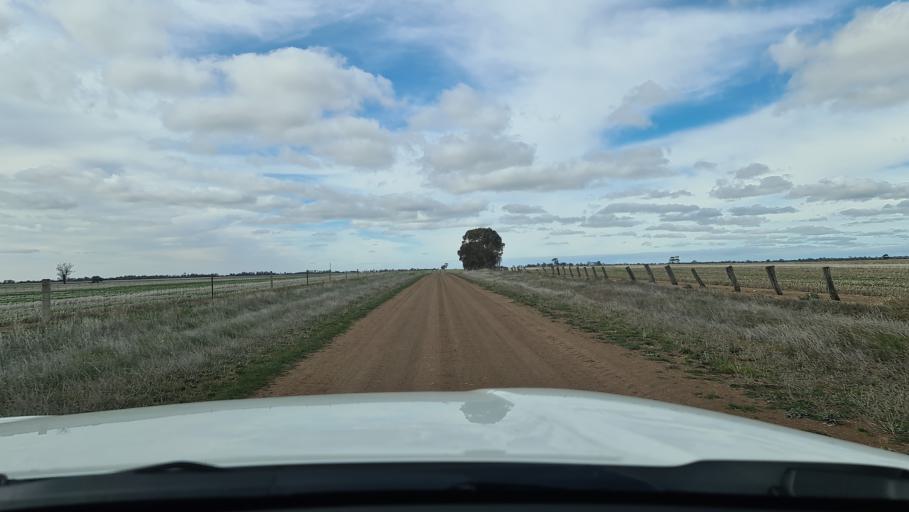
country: AU
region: Victoria
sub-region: Horsham
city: Horsham
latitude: -36.6313
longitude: 142.4275
